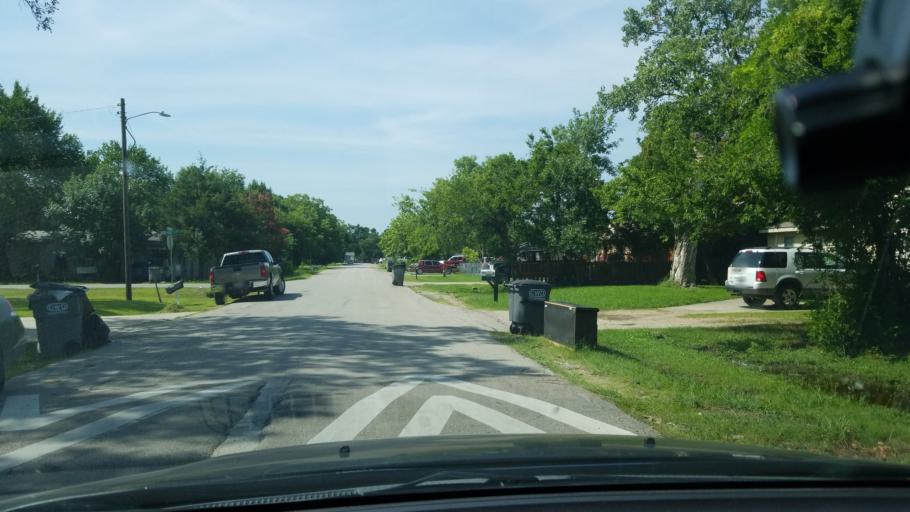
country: US
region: Texas
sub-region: Dallas County
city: Balch Springs
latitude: 32.7332
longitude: -96.6264
